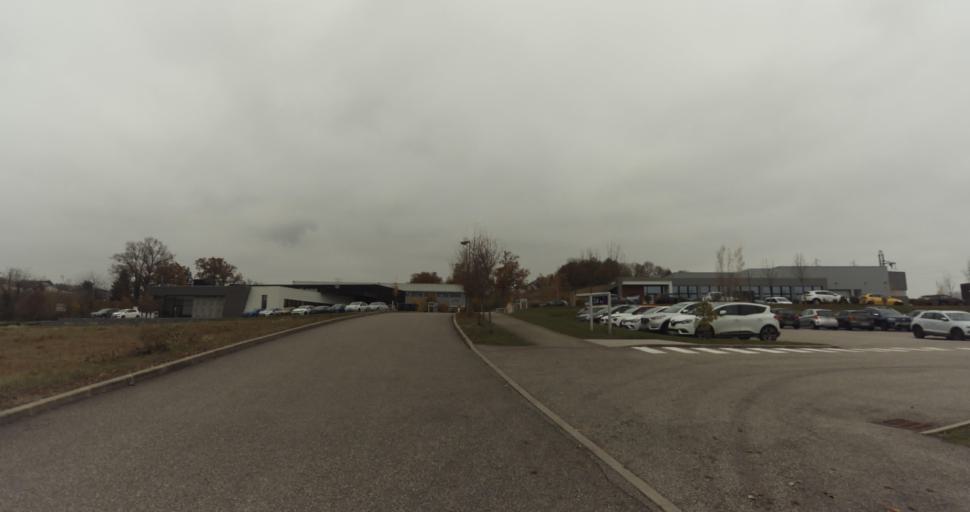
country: FR
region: Rhone-Alpes
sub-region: Departement de la Haute-Savoie
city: Seynod
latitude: 45.8917
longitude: 6.0769
